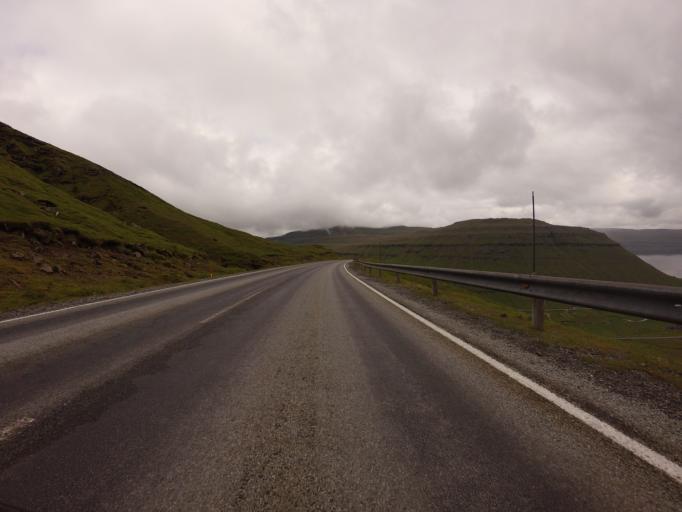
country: FO
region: Streymoy
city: Kollafjordhur
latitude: 62.0960
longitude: -6.9739
